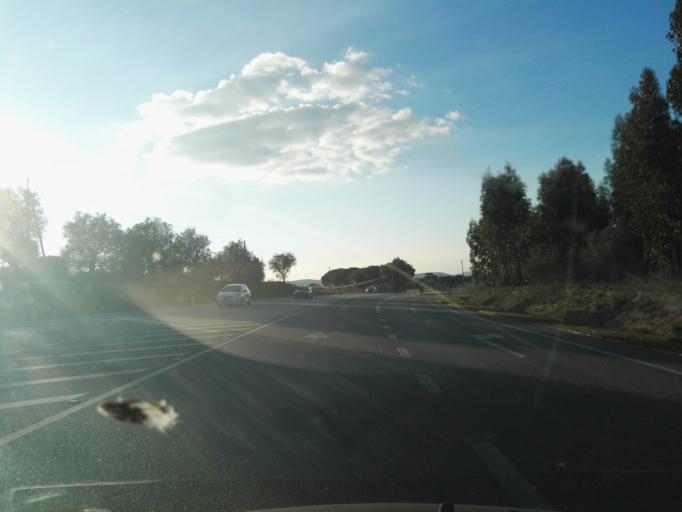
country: PT
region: Evora
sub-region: Arraiolos
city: Arraiolos
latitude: 38.6036
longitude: -8.0504
